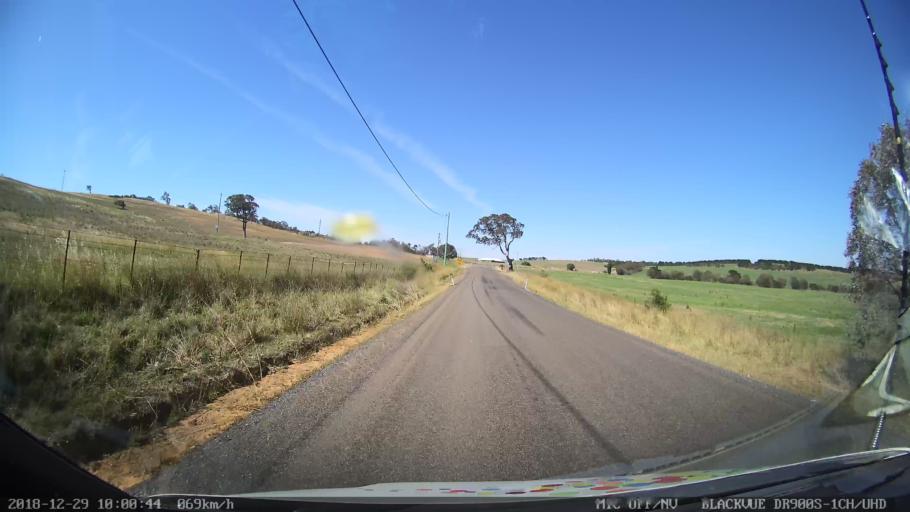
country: AU
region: New South Wales
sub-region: Goulburn Mulwaree
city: Goulburn
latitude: -34.7947
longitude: 149.4836
